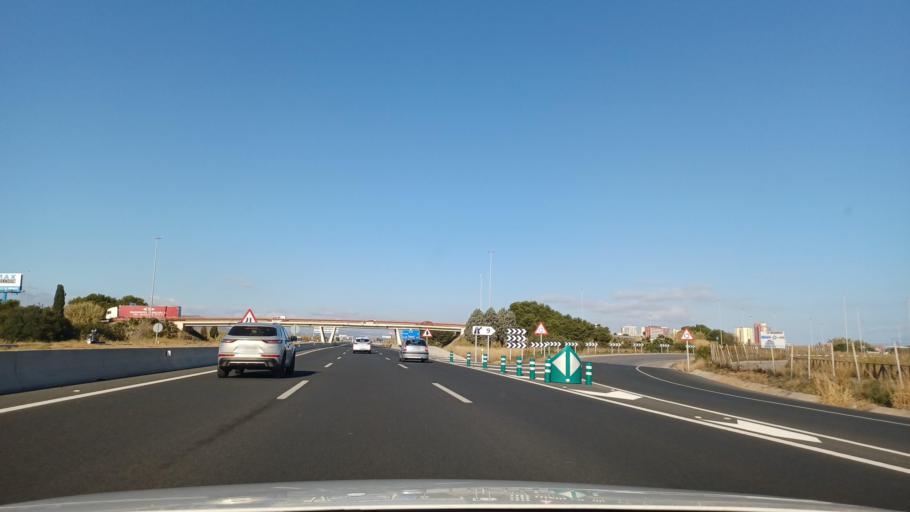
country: ES
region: Valencia
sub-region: Provincia de Valencia
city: Albuixech
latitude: 39.5498
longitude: -0.2978
